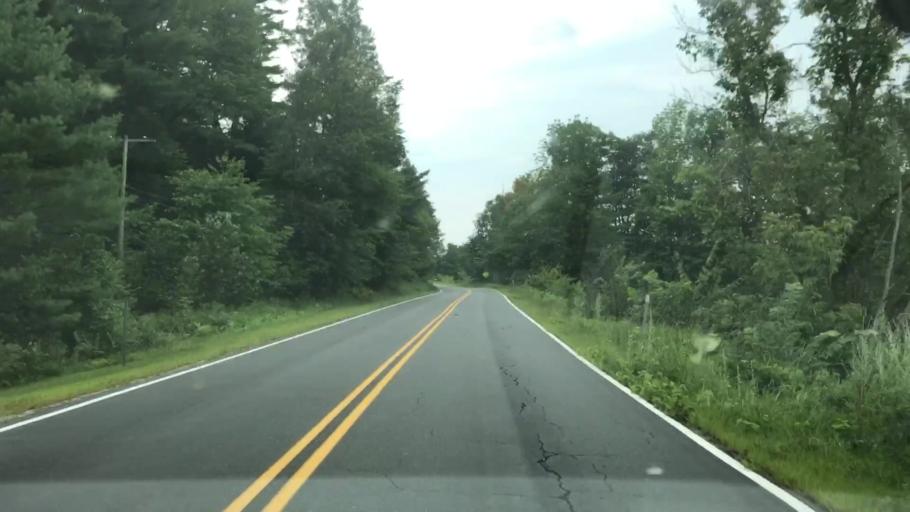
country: US
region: New Hampshire
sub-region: Grafton County
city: Woodsville
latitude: 44.2267
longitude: -72.0468
